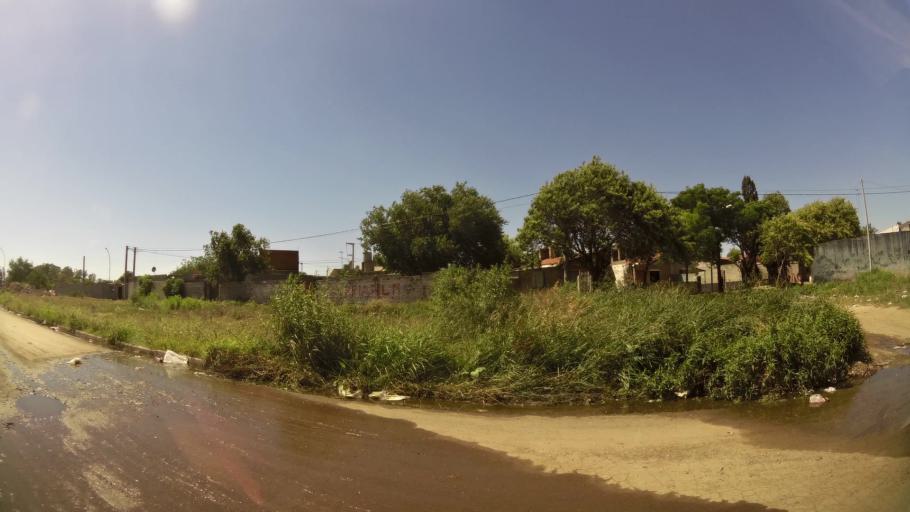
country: AR
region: Cordoba
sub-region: Departamento de Capital
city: Cordoba
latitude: -31.4072
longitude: -64.1385
